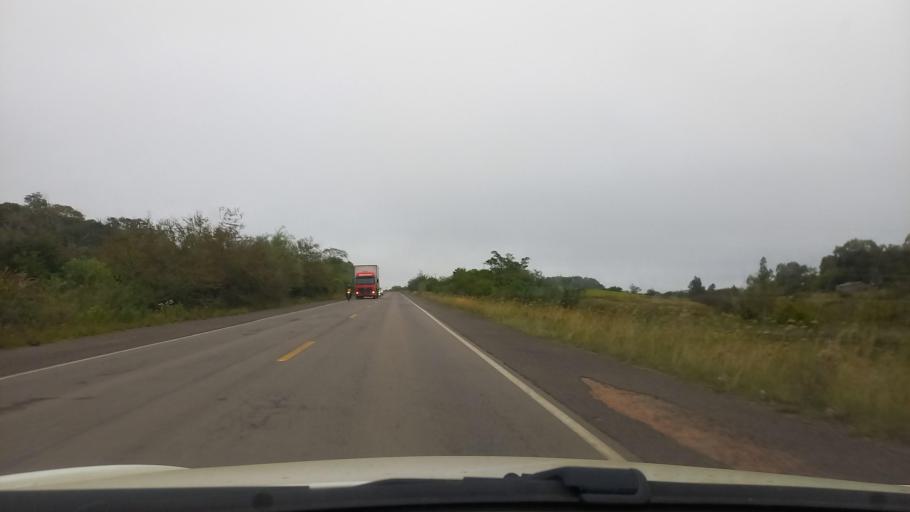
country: BR
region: Rio Grande do Sul
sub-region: Cacequi
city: Cacequi
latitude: -30.1235
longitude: -54.6469
